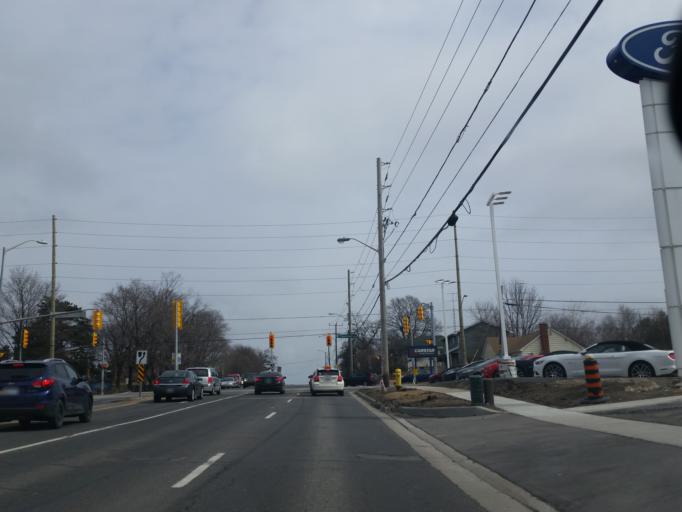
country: CA
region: Ontario
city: Oshawa
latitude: 43.8907
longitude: -78.8941
